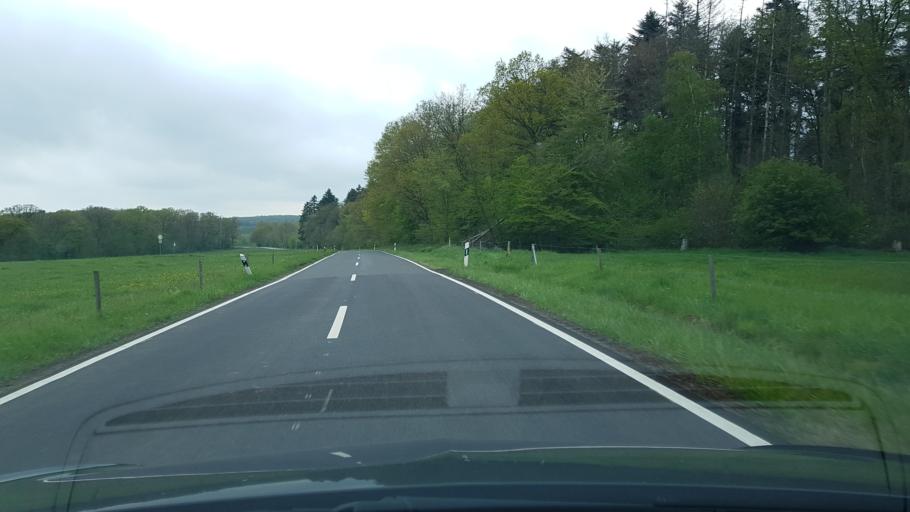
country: DE
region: Rheinland-Pfalz
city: Nortershausen
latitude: 50.2512
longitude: 7.4967
